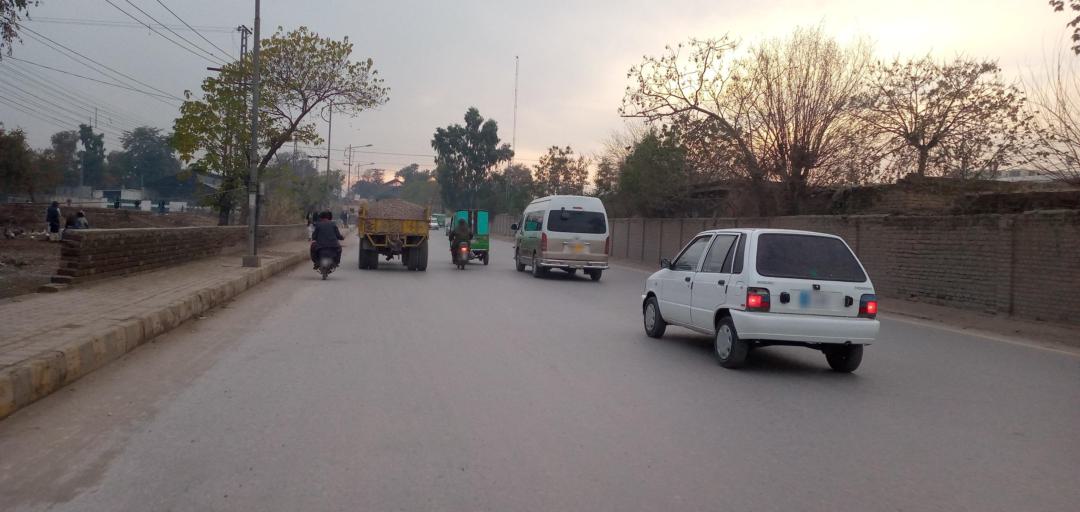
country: PK
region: Khyber Pakhtunkhwa
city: Peshawar
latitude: 34.0002
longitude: 71.5496
